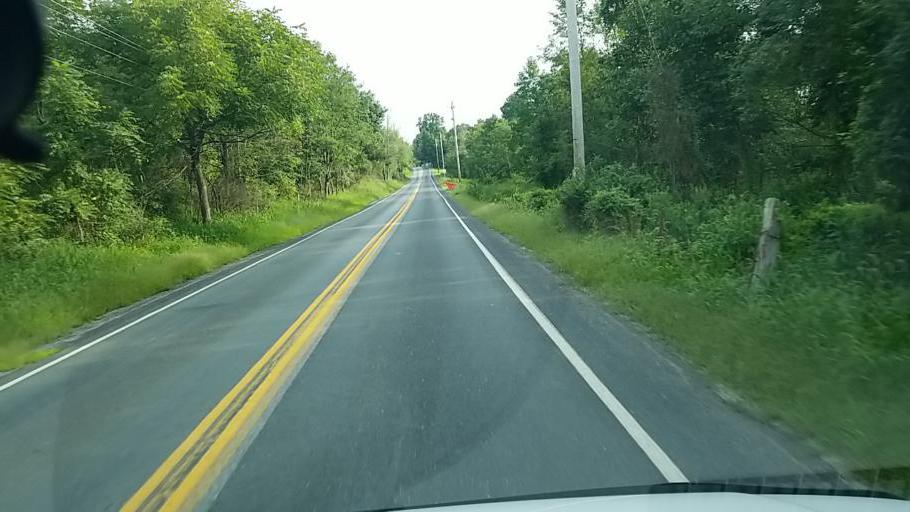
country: US
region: Pennsylvania
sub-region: Cumberland County
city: Newville
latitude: 40.2542
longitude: -77.4424
